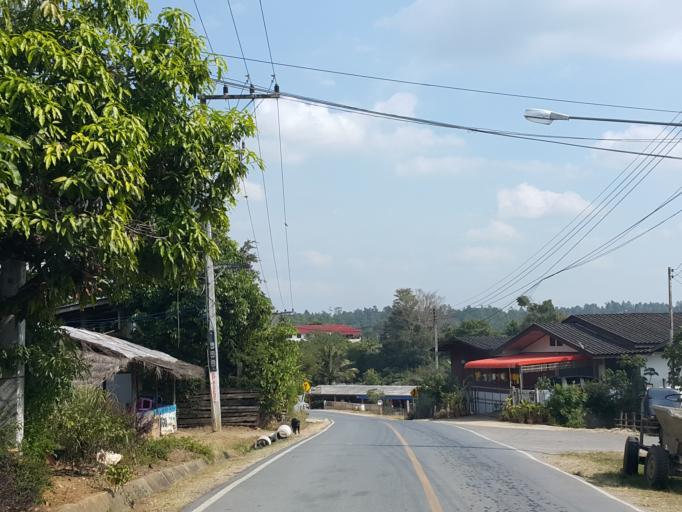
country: TH
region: Chiang Mai
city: Om Koi
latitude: 17.7979
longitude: 98.3588
